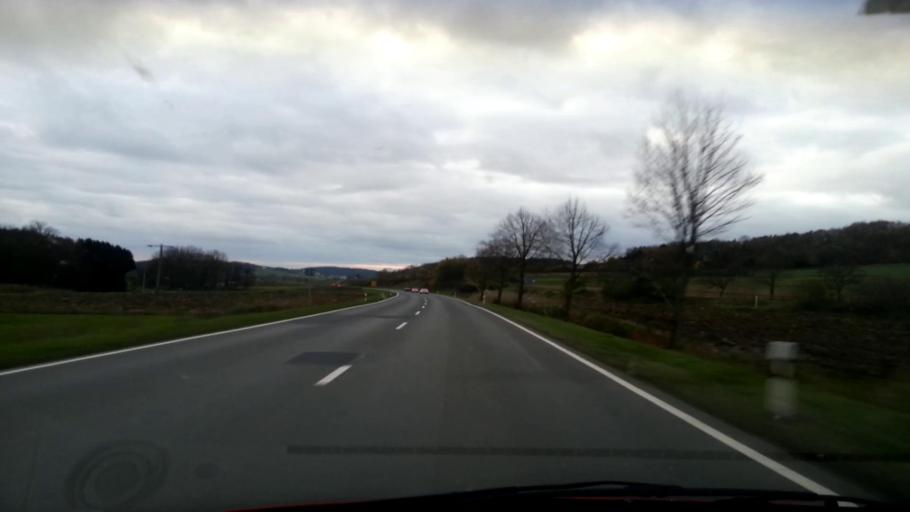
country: DE
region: Bavaria
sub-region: Upper Franconia
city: Kueps Oberfranken
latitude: 50.2131
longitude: 11.2392
